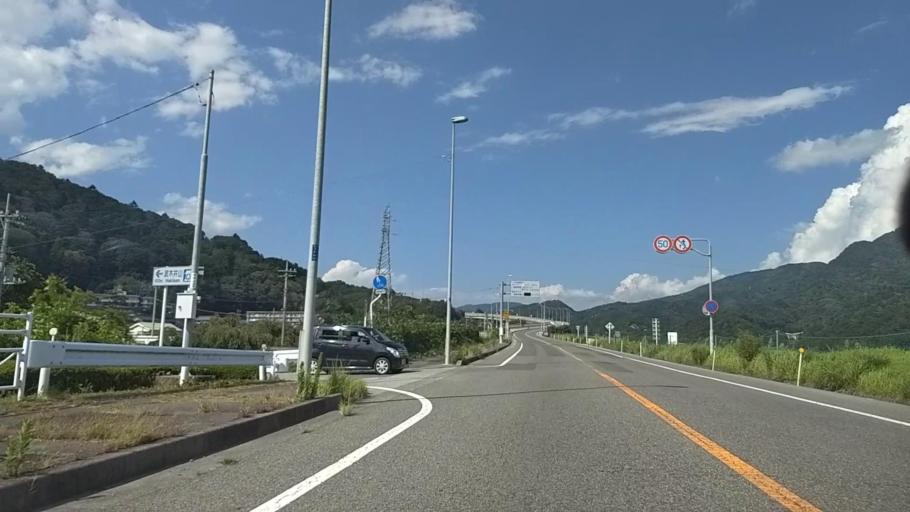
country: JP
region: Shizuoka
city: Fujinomiya
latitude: 35.3754
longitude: 138.4475
